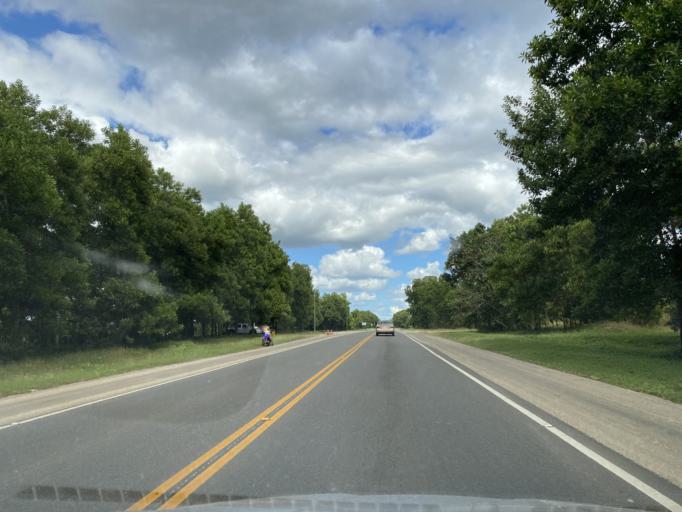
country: DO
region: Santo Domingo
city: Guerra
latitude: 18.6483
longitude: -69.7523
